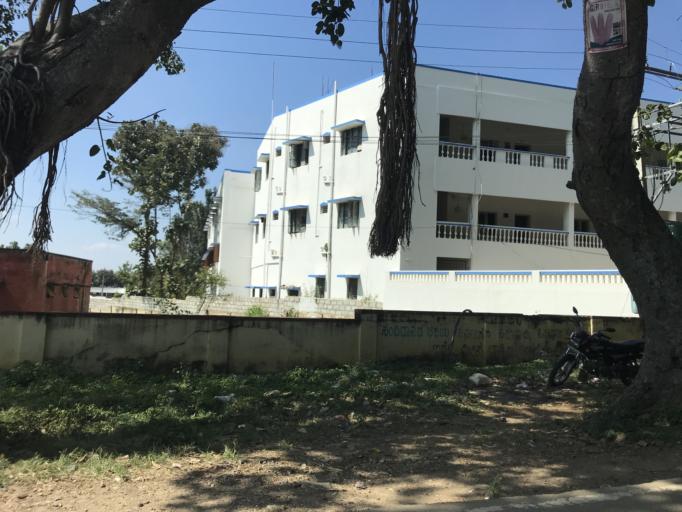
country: IN
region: Karnataka
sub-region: Mysore
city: Heggadadevankote
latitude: 12.0935
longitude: 76.3320
